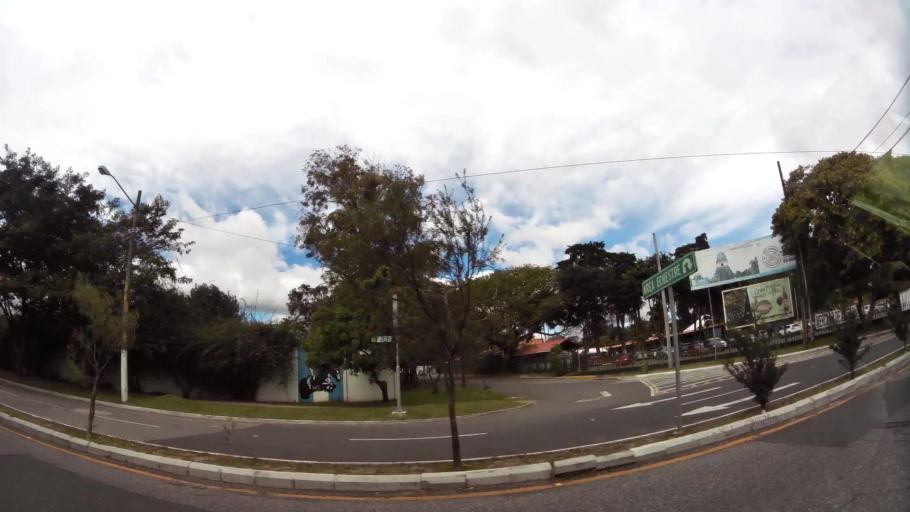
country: GT
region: Guatemala
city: Santa Catarina Pinula
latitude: 14.5959
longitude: -90.5259
